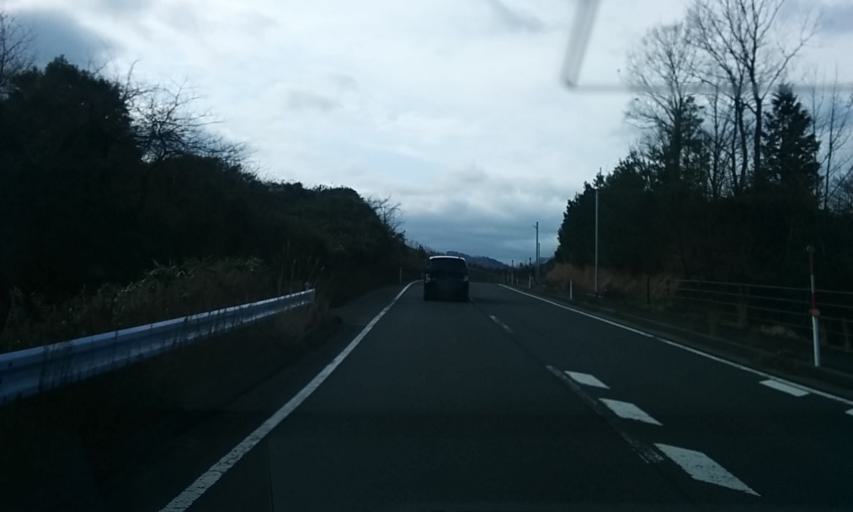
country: JP
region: Kyoto
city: Miyazu
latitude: 35.5831
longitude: 135.1054
